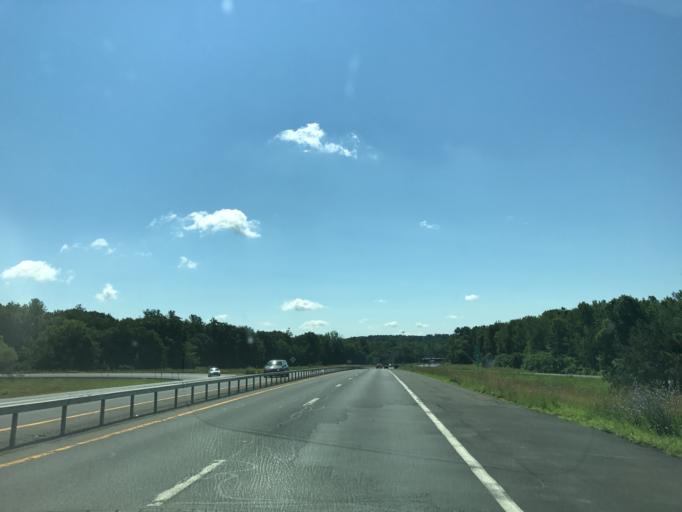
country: US
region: New York
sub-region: Columbia County
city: Niverville
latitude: 42.4891
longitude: -73.6774
